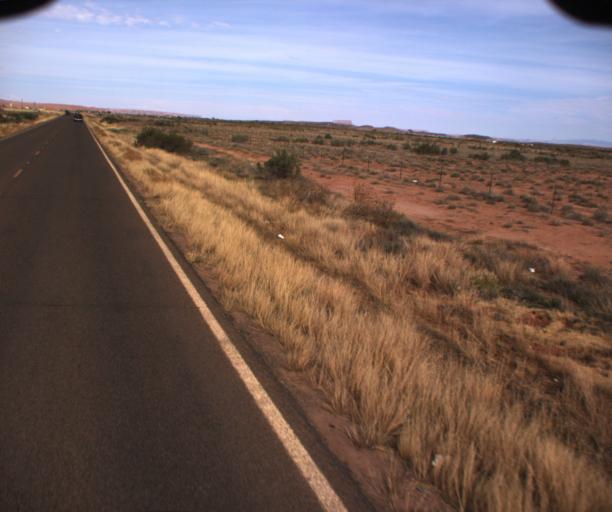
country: US
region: Arizona
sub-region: Apache County
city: Many Farms
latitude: 36.3032
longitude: -109.6079
